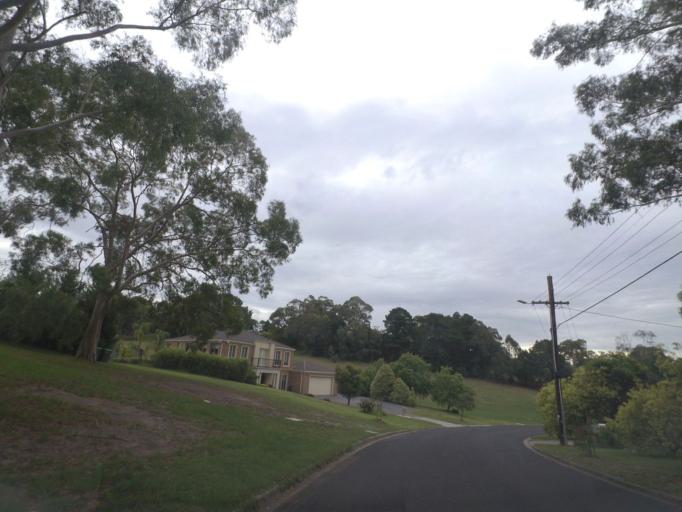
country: AU
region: Victoria
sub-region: Manningham
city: Donvale
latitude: -37.7987
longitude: 145.1914
